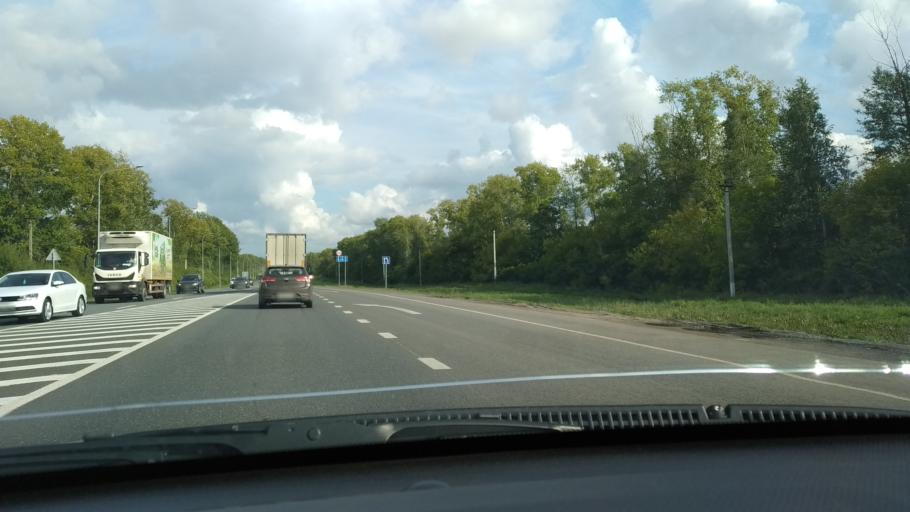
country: RU
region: Tatarstan
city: Stolbishchi
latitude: 55.6553
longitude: 49.3131
